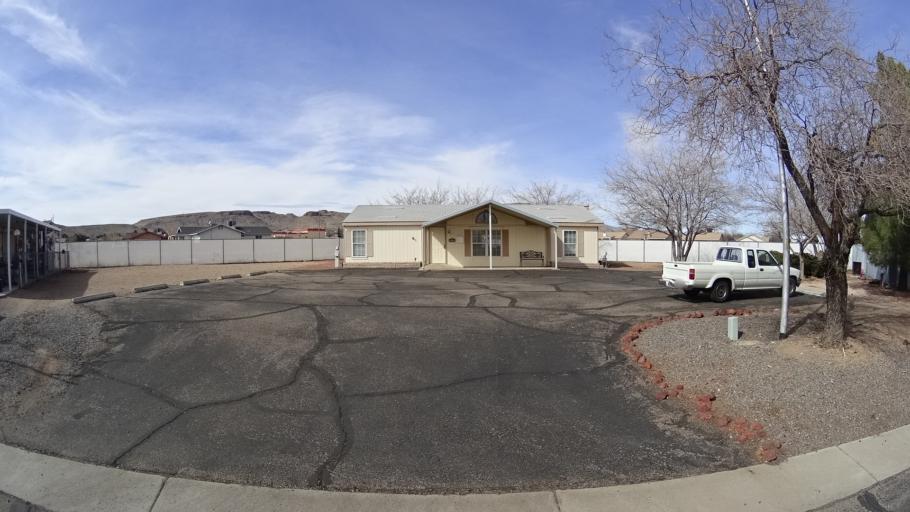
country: US
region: Arizona
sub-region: Mohave County
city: New Kingman-Butler
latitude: 35.2308
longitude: -114.0310
